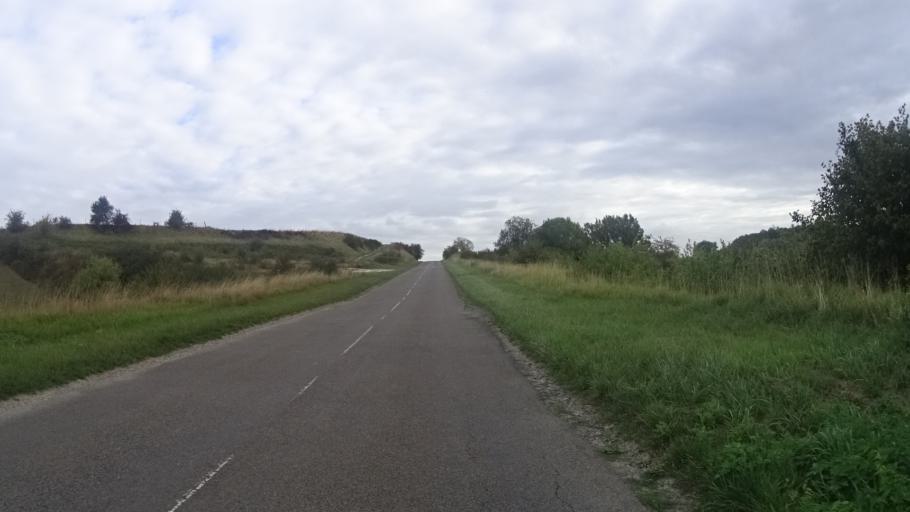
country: FR
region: Picardie
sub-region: Departement de l'Aisne
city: Guise
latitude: 49.9459
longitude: 3.5878
